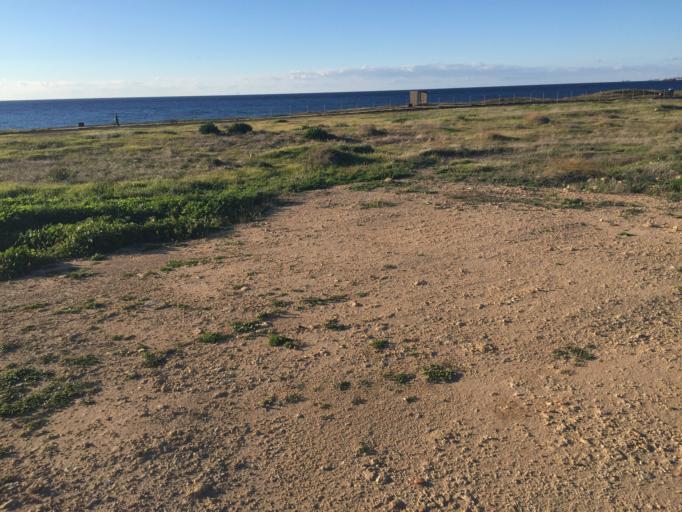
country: CY
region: Pafos
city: Paphos
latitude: 34.7569
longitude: 32.4035
